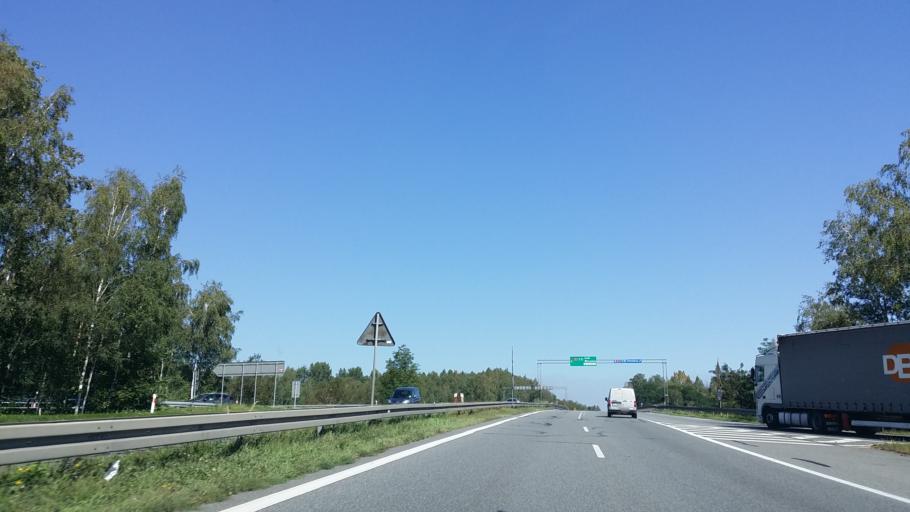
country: PL
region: Silesian Voivodeship
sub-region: Myslowice
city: Myslowice
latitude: 50.2063
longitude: 19.1662
